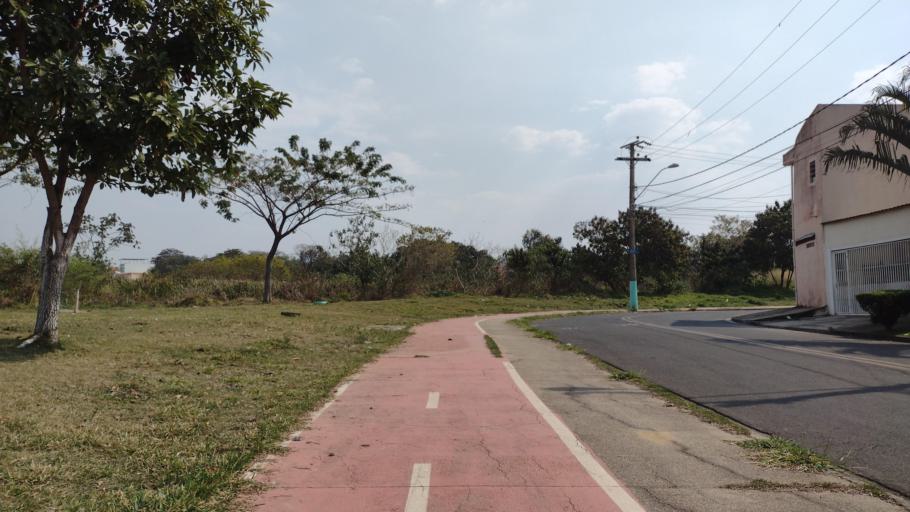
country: BR
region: Sao Paulo
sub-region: Sorocaba
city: Sorocaba
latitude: -23.4354
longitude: -47.4600
